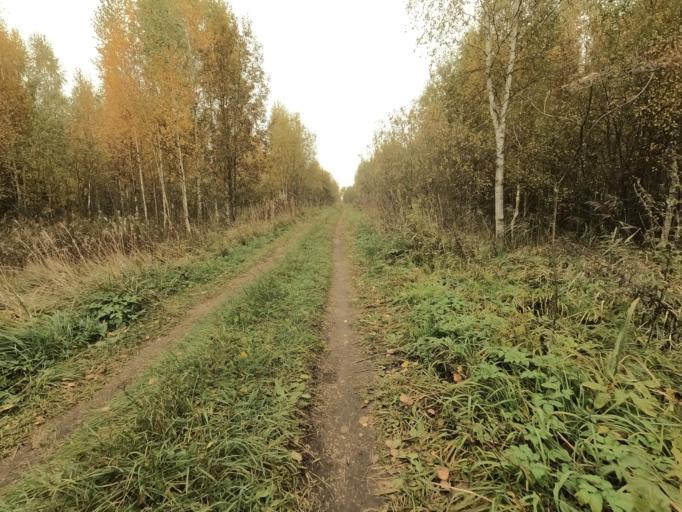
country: RU
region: Novgorod
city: Pankovka
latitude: 58.8791
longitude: 30.9422
